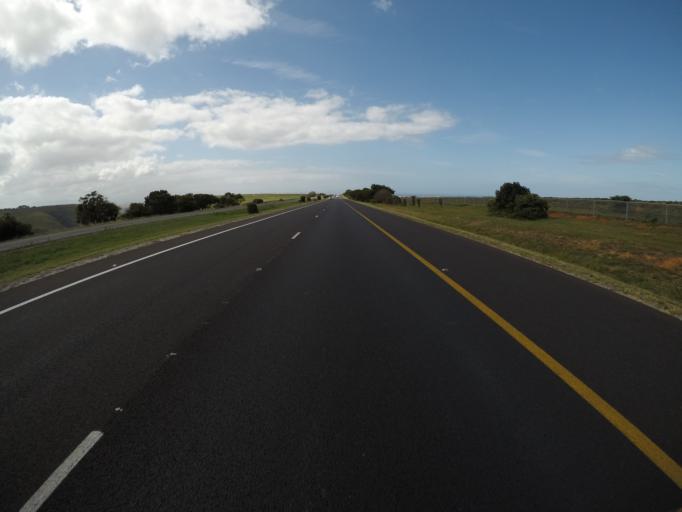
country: ZA
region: Western Cape
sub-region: Eden District Municipality
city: Mossel Bay
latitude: -34.1672
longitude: 22.0828
